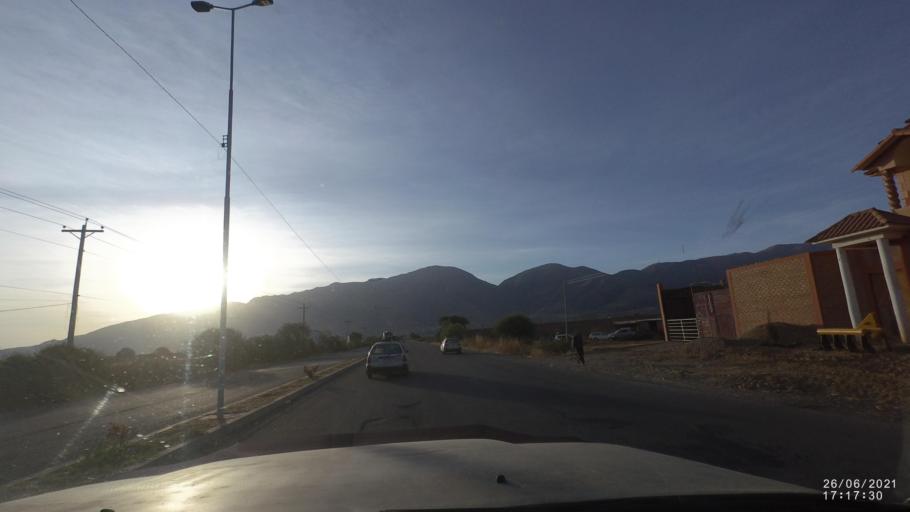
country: BO
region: Cochabamba
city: Cliza
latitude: -17.5475
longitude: -65.9515
